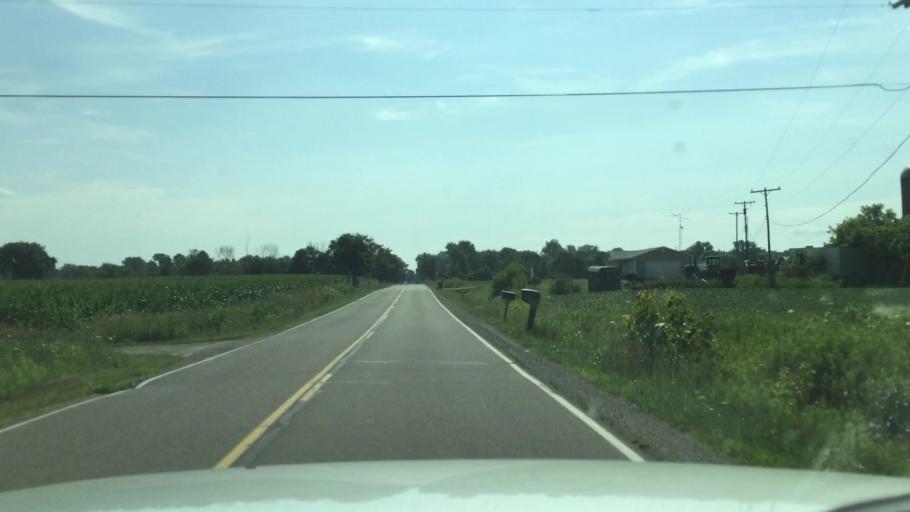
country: US
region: Michigan
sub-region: Genesee County
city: Flushing
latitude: 43.1335
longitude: -83.8229
